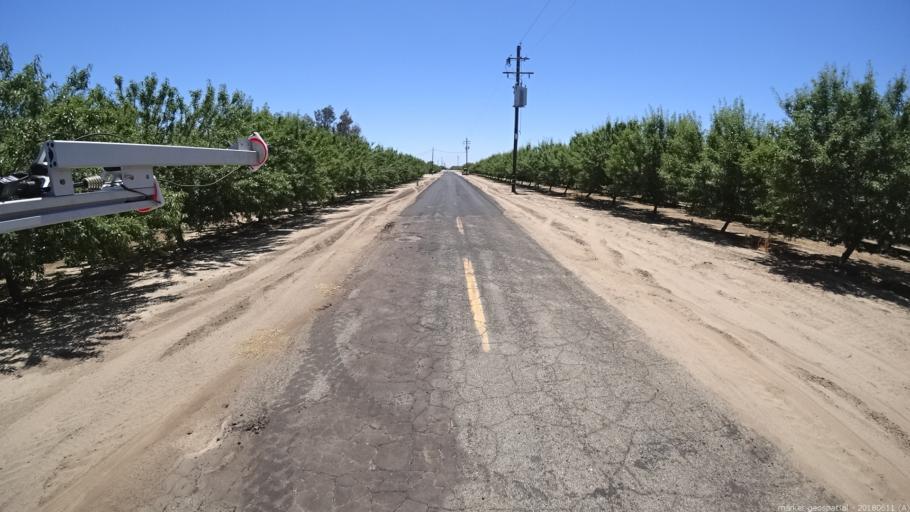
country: US
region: California
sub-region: Madera County
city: Fairmead
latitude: 37.0059
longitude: -120.1933
